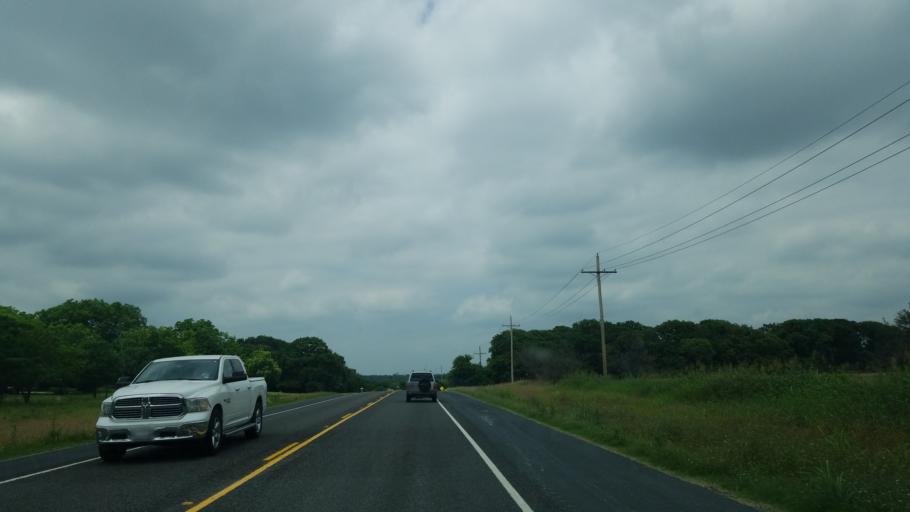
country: US
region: Texas
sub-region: Denton County
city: Pilot Point
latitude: 33.4413
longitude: -96.9262
